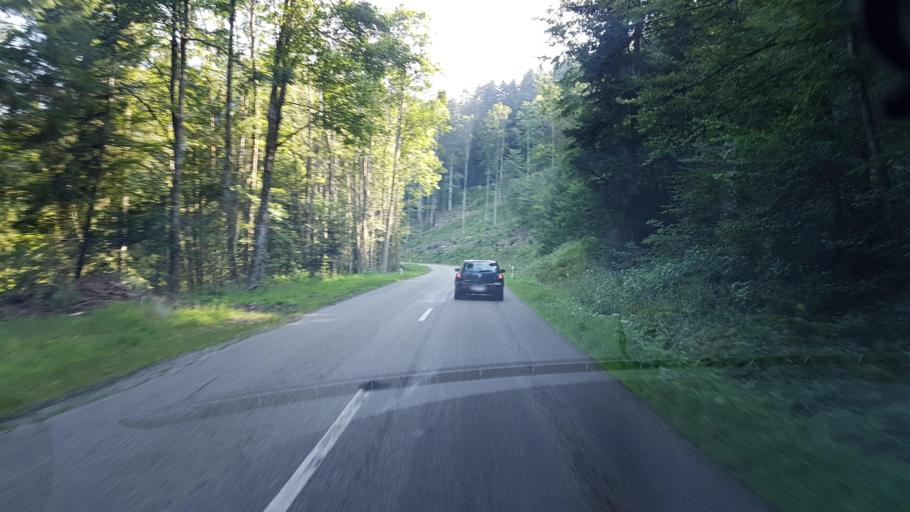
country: DE
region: Baden-Wuerttemberg
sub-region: Freiburg Region
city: Hochenschwand
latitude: 47.7254
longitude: 8.1419
